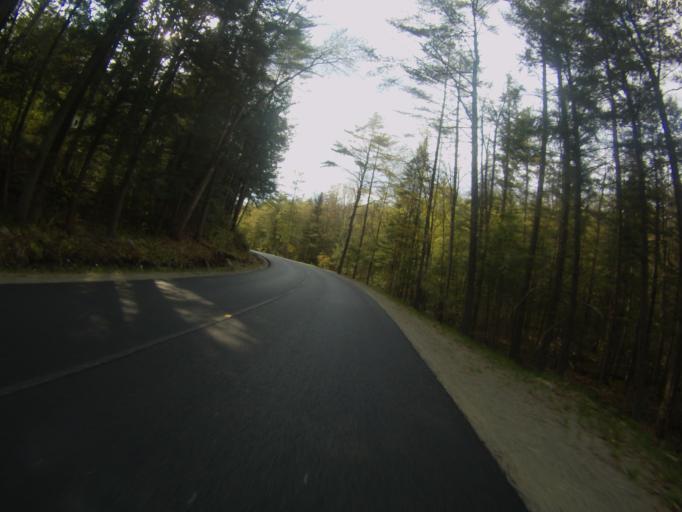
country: US
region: New York
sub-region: Warren County
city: Warrensburg
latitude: 43.8410
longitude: -73.7844
